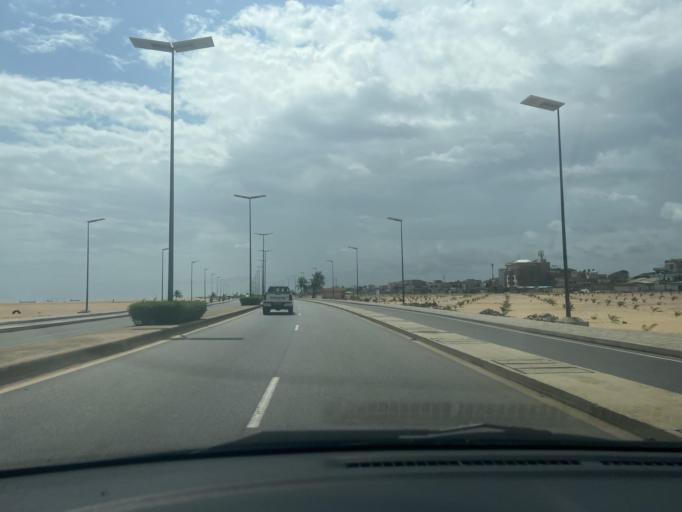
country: BJ
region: Littoral
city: Cotonou
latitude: 6.3488
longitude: 2.3718
